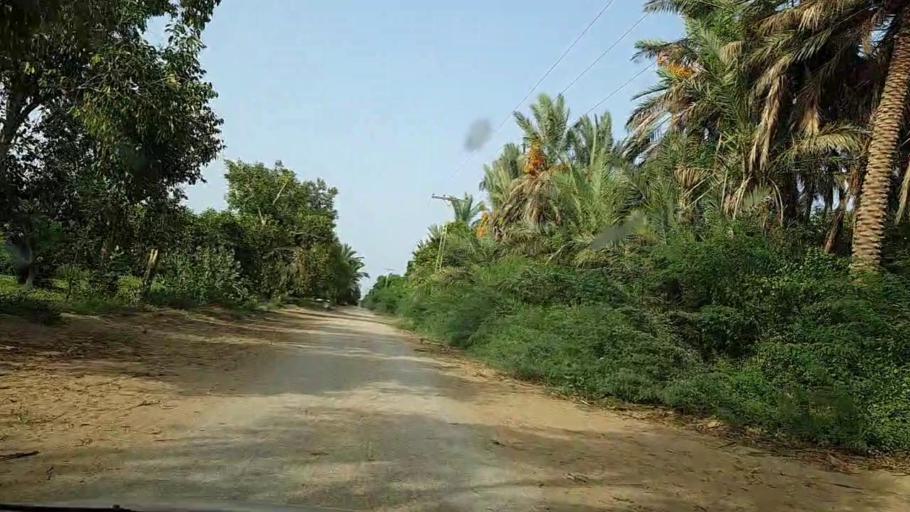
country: PK
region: Sindh
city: Kotri
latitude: 25.2248
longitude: 68.2509
